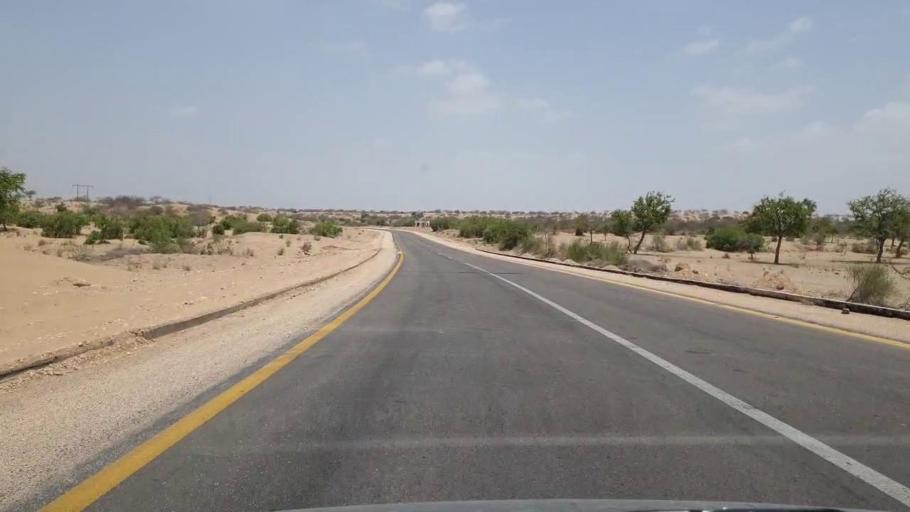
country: PK
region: Sindh
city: Mithi
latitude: 24.8195
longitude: 69.7016
